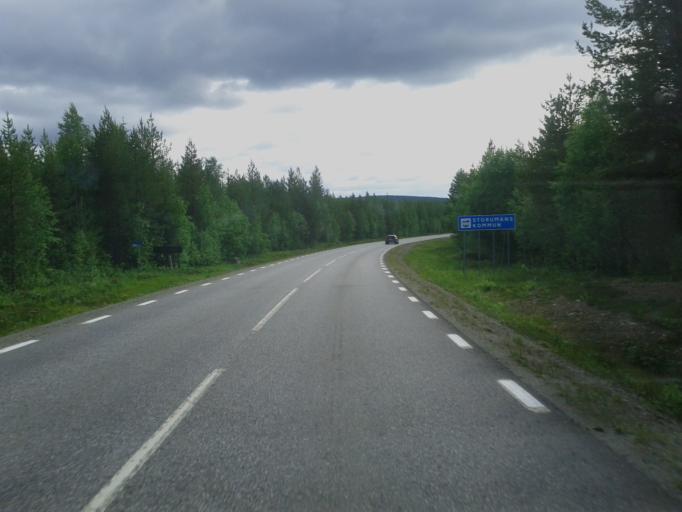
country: SE
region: Vaesterbotten
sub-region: Sorsele Kommun
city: Sorsele
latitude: 65.1913
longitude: 17.5903
